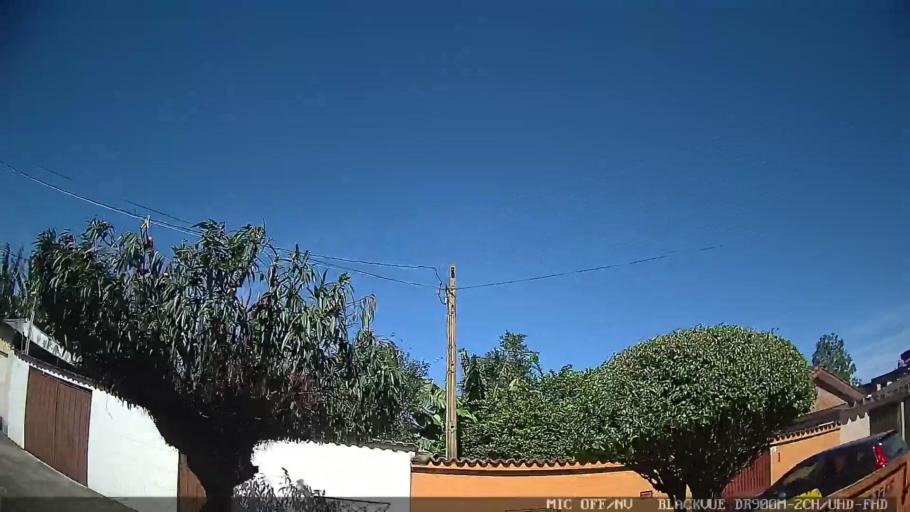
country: BR
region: Sao Paulo
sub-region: Guaruja
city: Guaruja
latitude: -23.9651
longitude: -46.2776
